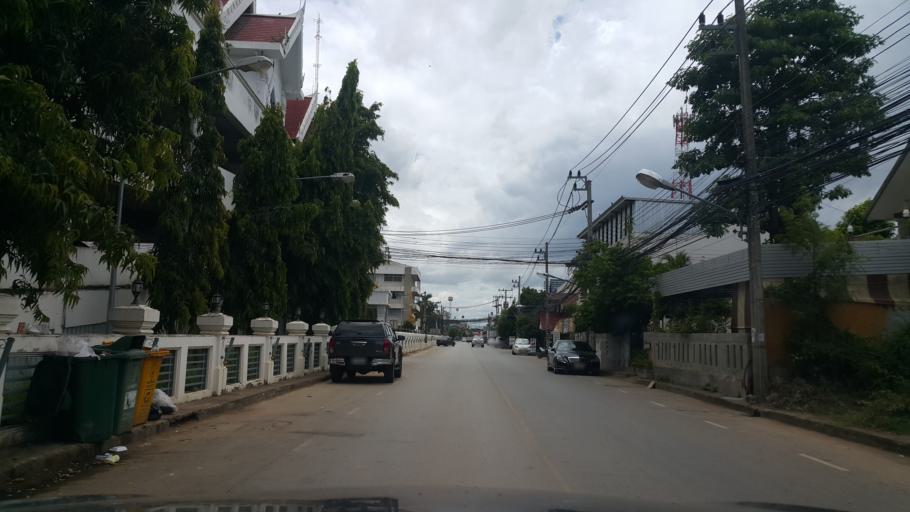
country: TH
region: Sukhothai
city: Sukhothai
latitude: 17.0059
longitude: 99.8275
